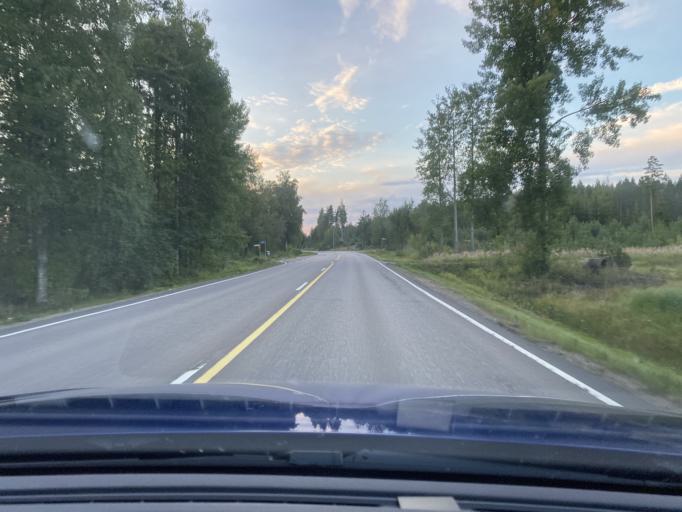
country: FI
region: Satakunta
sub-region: Pohjois-Satakunta
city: Honkajoki
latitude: 61.9313
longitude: 22.2416
